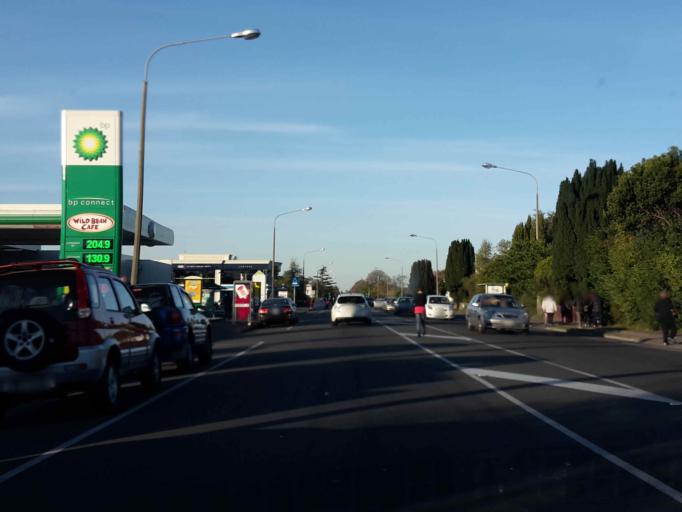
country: NZ
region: Canterbury
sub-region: Christchurch City
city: Christchurch
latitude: -43.5316
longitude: 172.5756
